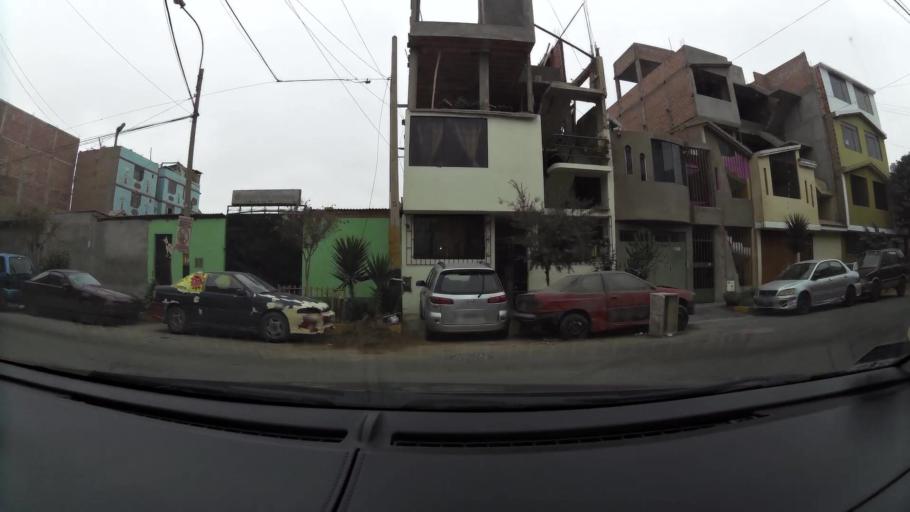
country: PE
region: Lima
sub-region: Lima
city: Independencia
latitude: -11.9620
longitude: -77.0747
